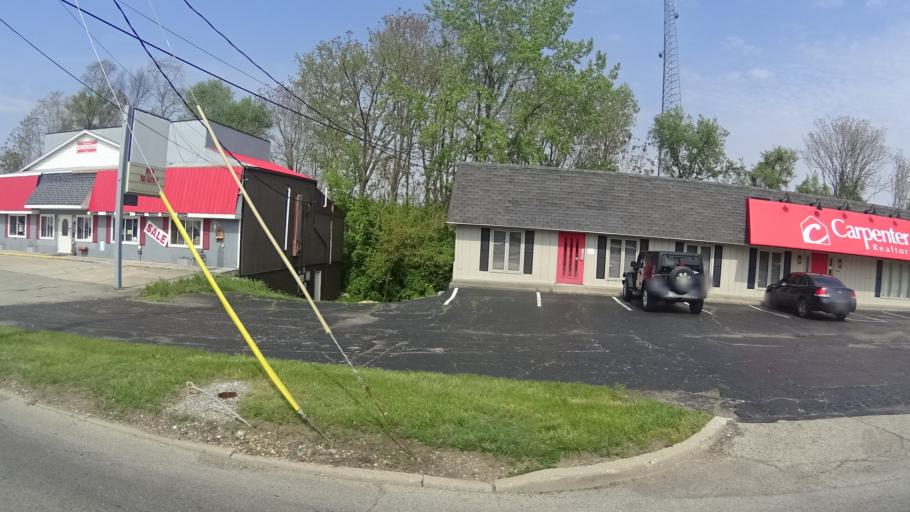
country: US
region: Indiana
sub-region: Madison County
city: Anderson
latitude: 40.1159
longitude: -85.6799
